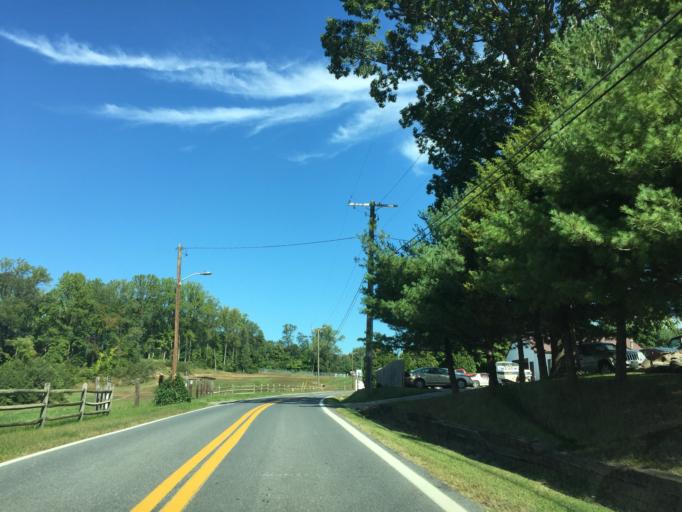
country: US
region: Maryland
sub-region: Baltimore County
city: White Marsh
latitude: 39.3974
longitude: -76.4112
